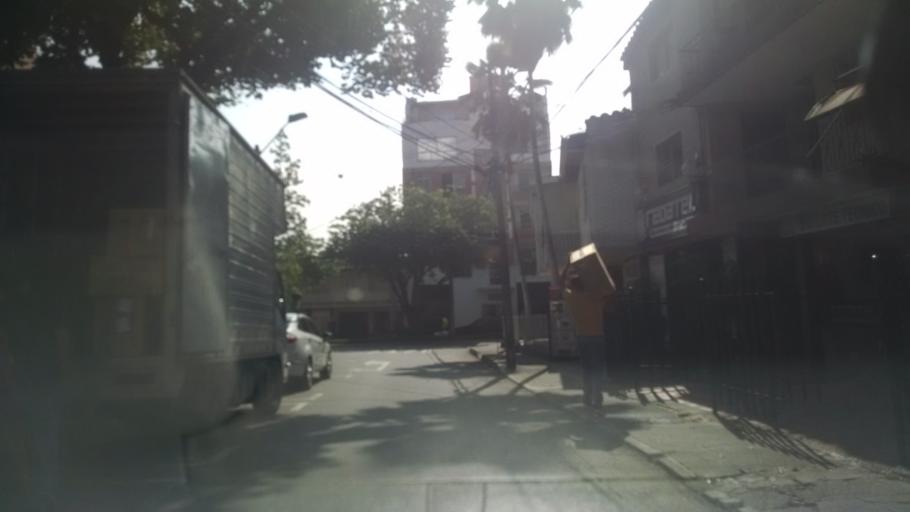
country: CO
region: Antioquia
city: Medellin
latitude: 6.2463
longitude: -75.5886
